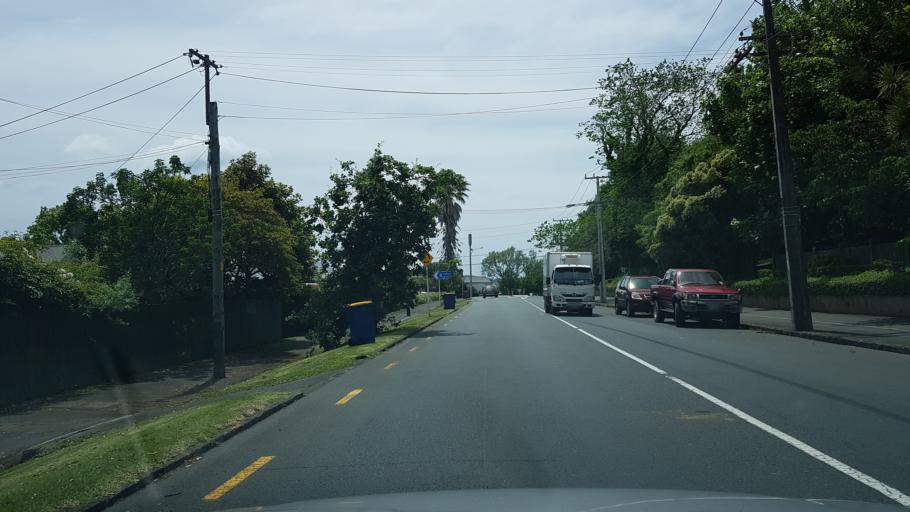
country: NZ
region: Auckland
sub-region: Auckland
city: Auckland
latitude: -36.8253
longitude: 174.7974
